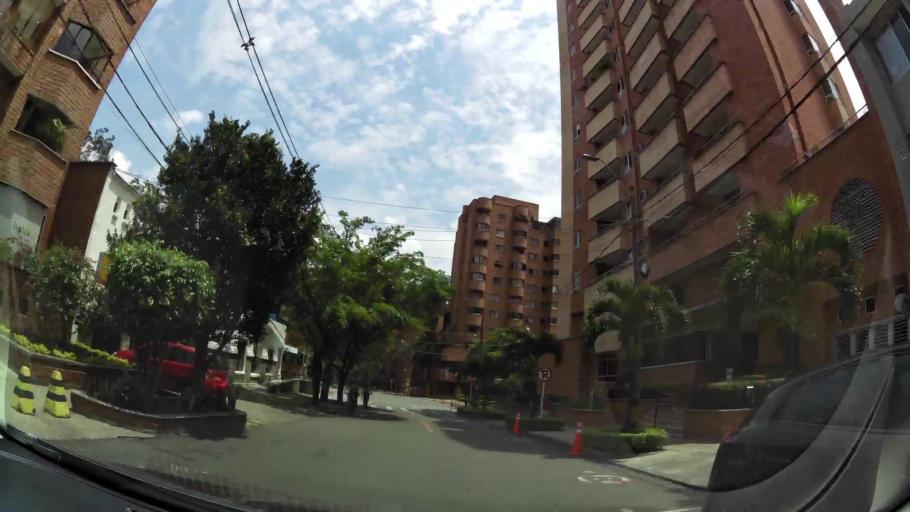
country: CO
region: Antioquia
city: Medellin
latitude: 6.2433
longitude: -75.5974
